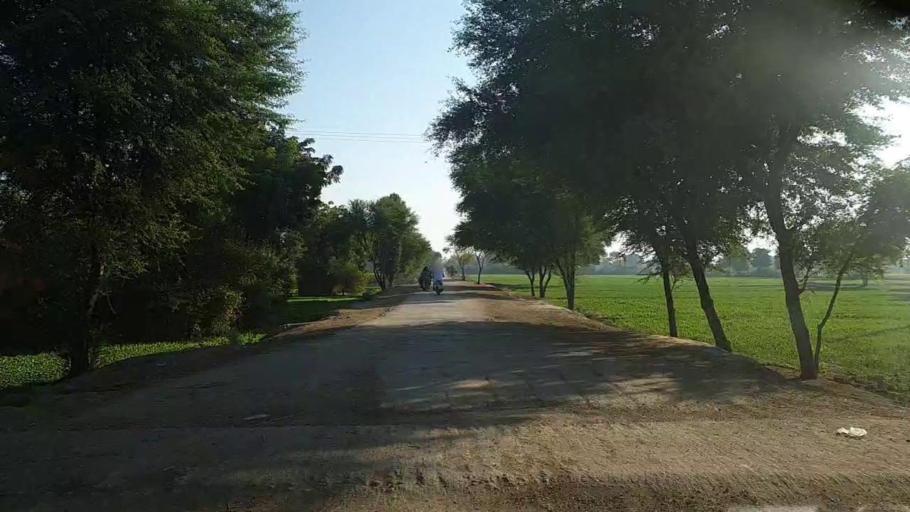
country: PK
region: Sindh
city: Darya Khan Marri
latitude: 26.7002
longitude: 68.3625
